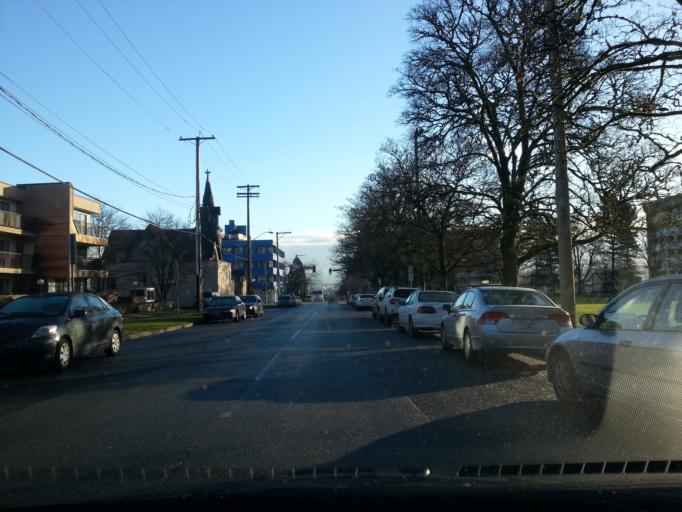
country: CA
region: British Columbia
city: New Westminster
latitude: 49.2279
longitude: -122.8944
